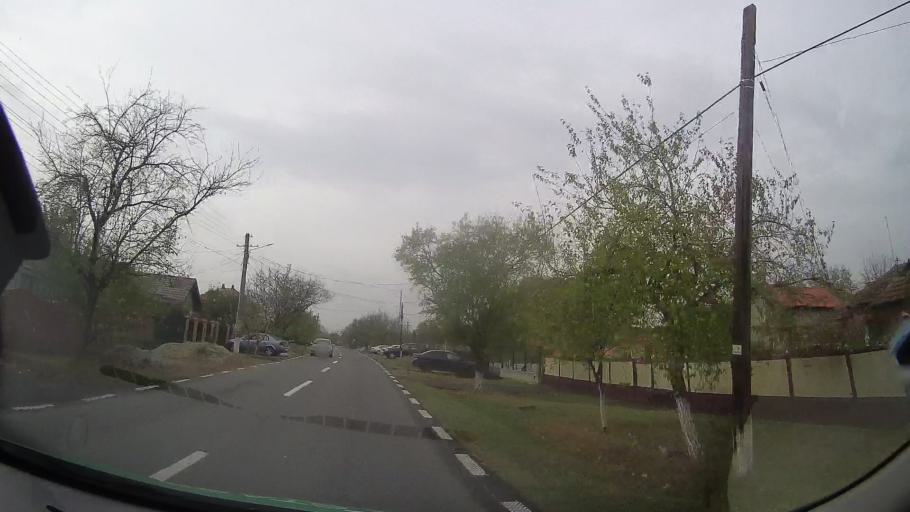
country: RO
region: Ilfov
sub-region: Comuna Gruiu
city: Lipia
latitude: 44.7147
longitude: 26.2553
